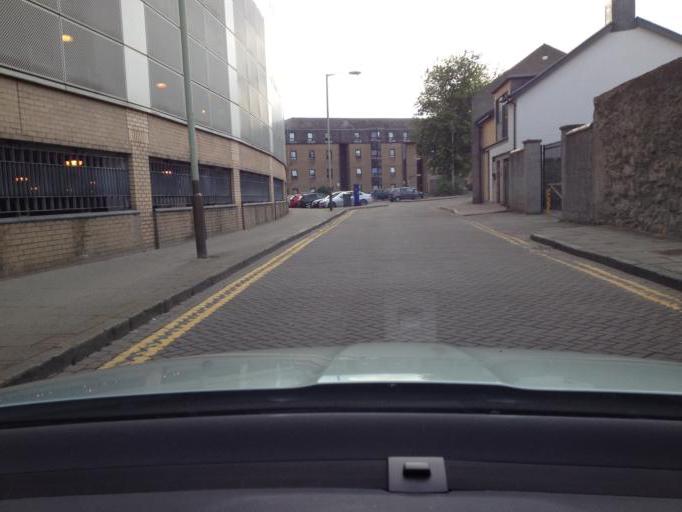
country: GB
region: Scotland
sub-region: Perth and Kinross
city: Perth
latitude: 56.3982
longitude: -3.4303
